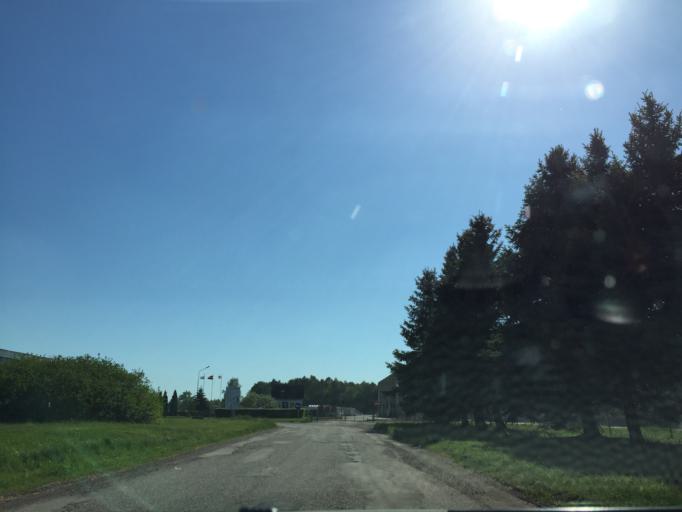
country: LV
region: Ozolnieku
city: Ozolnieki
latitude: 56.6659
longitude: 23.8043
